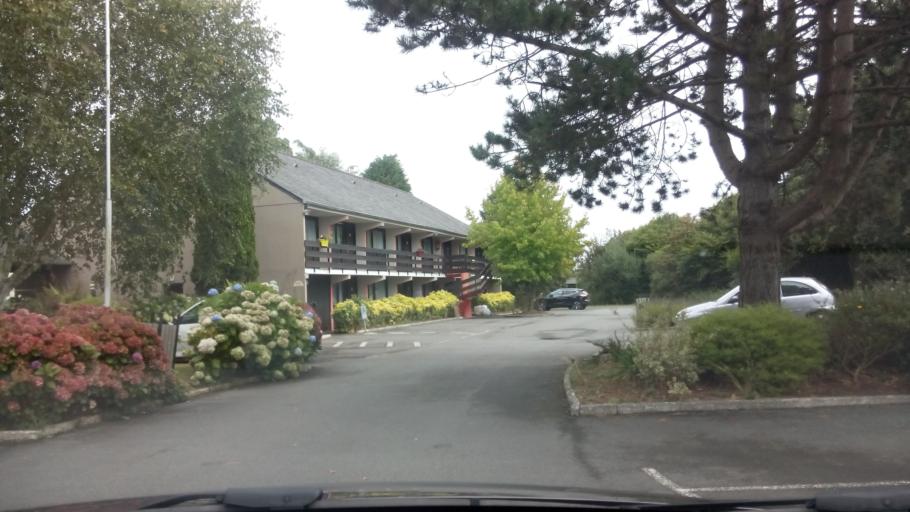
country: FR
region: Brittany
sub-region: Departement des Cotes-d'Armor
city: Lannion
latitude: 48.7491
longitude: -3.4580
